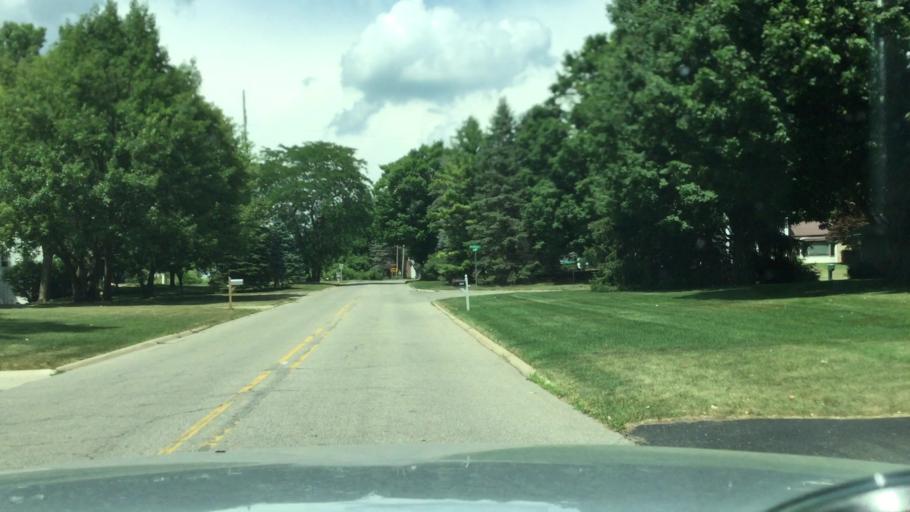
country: US
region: Michigan
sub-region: Genesee County
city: Flushing
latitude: 43.0443
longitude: -83.7876
